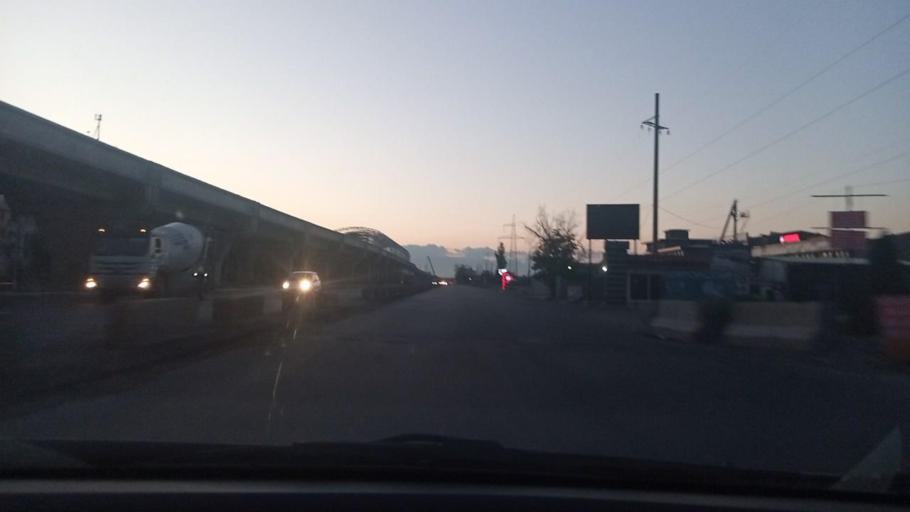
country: UZ
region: Toshkent Shahri
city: Bektemir
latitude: 41.2442
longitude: 69.2964
